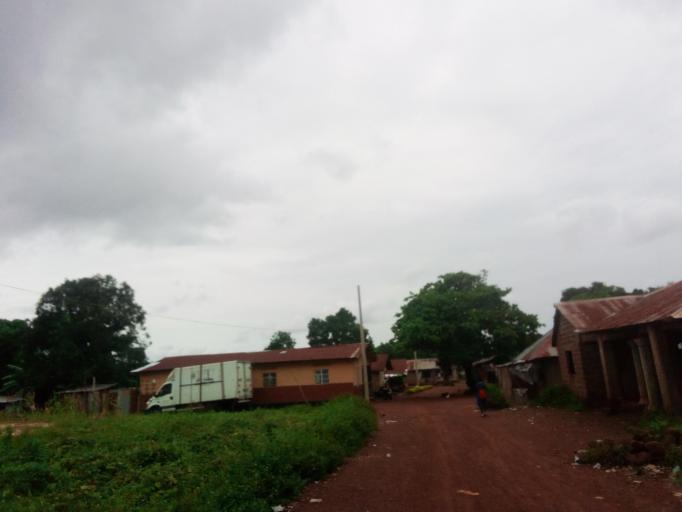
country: SL
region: Northern Province
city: Kambia
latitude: 9.1106
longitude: -12.9296
